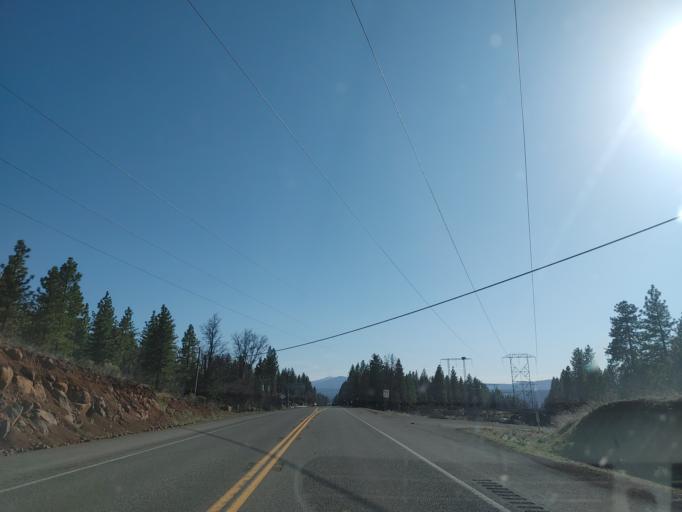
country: US
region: California
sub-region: Shasta County
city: Burney
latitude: 40.9264
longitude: -121.6191
